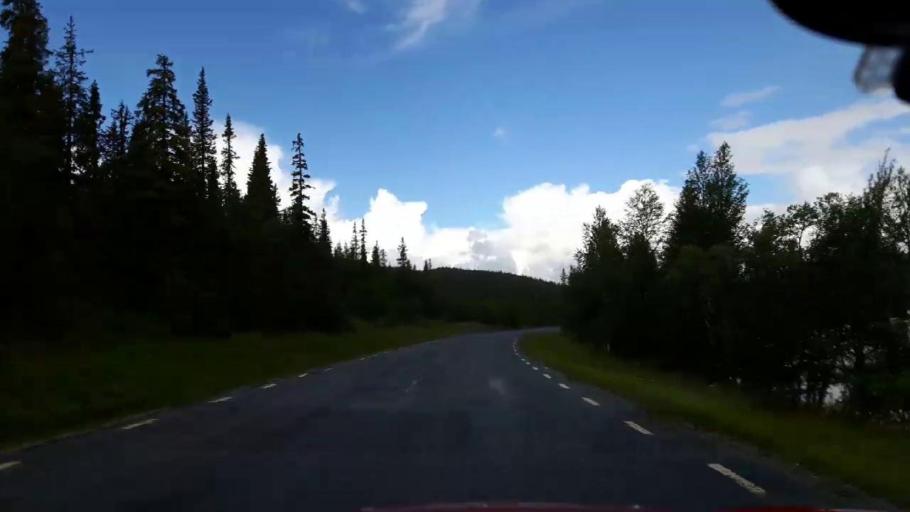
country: SE
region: Vaesterbotten
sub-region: Vilhelmina Kommun
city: Sjoberg
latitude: 65.0107
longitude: 15.1762
